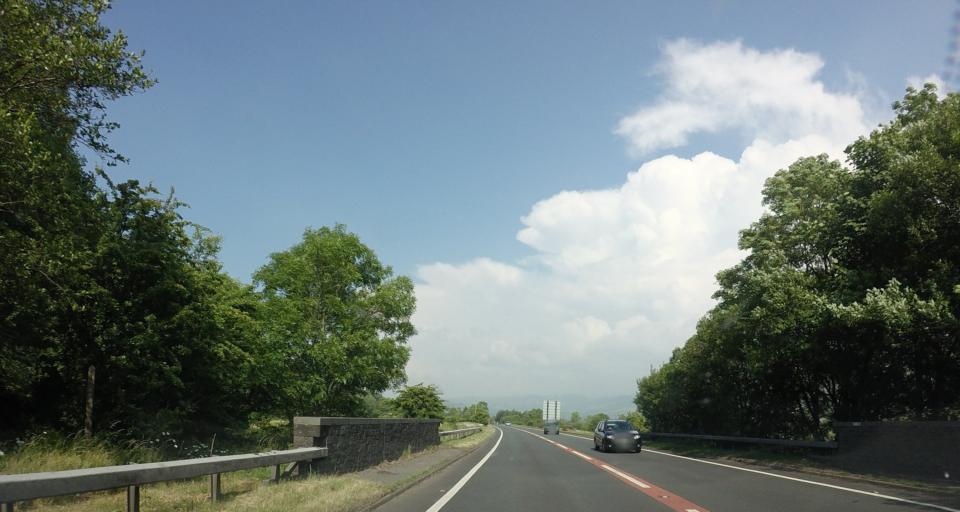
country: GB
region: England
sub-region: Cumbria
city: Cockermouth
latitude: 54.6620
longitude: -3.2785
